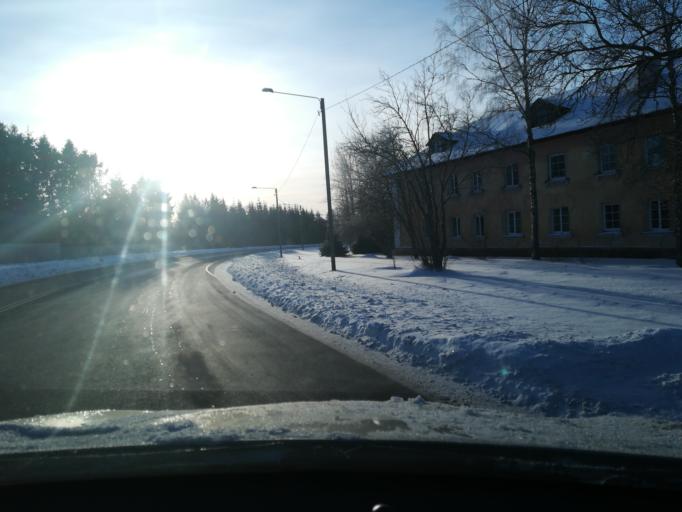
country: EE
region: Harju
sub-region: Keila linn
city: Keila
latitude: 59.3973
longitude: 24.3031
